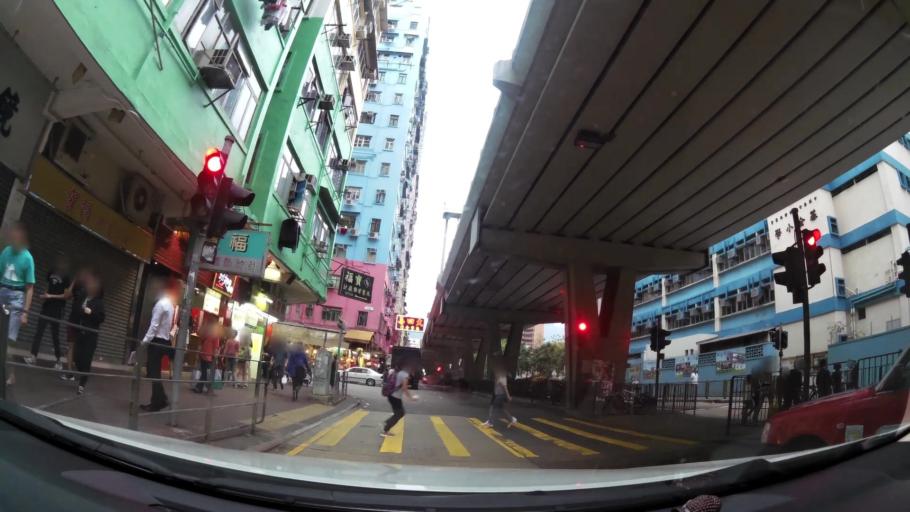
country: HK
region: Sham Shui Po
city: Sham Shui Po
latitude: 22.3223
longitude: 114.1619
